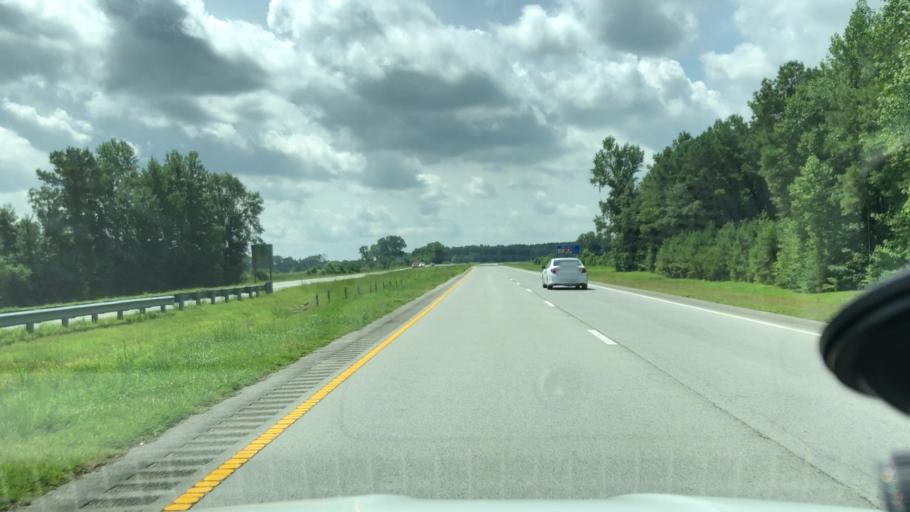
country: US
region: North Carolina
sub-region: Beaufort County
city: Washington
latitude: 35.5149
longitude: -77.0863
